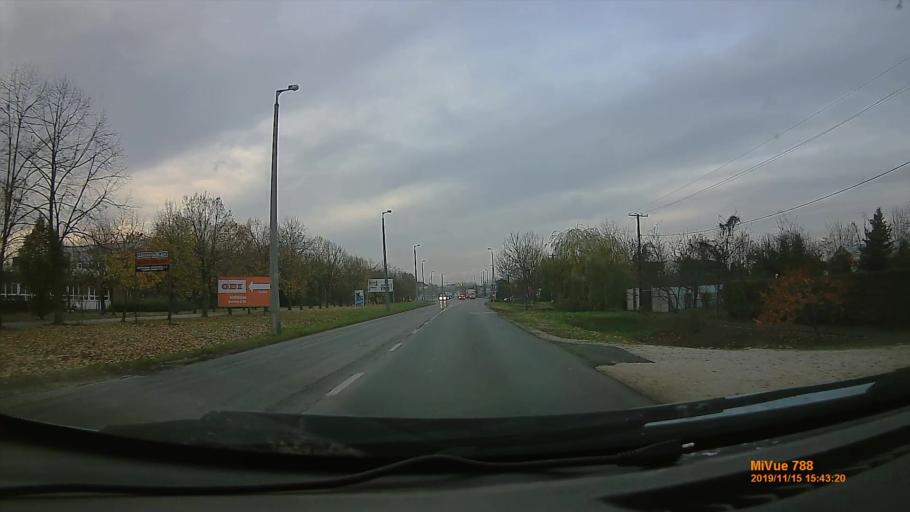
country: HU
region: Bekes
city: Bekescsaba
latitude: 46.6804
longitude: 21.1173
